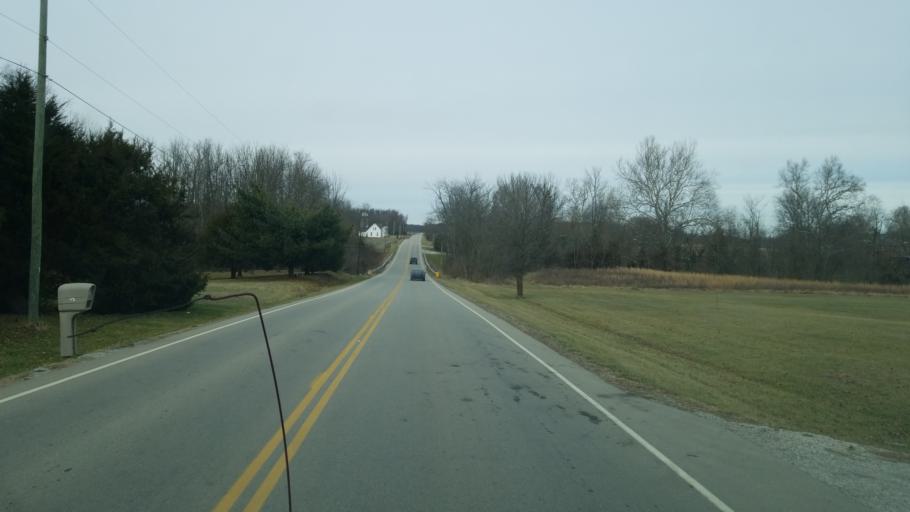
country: US
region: Ohio
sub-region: Adams County
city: Winchester
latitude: 39.0370
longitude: -83.7041
